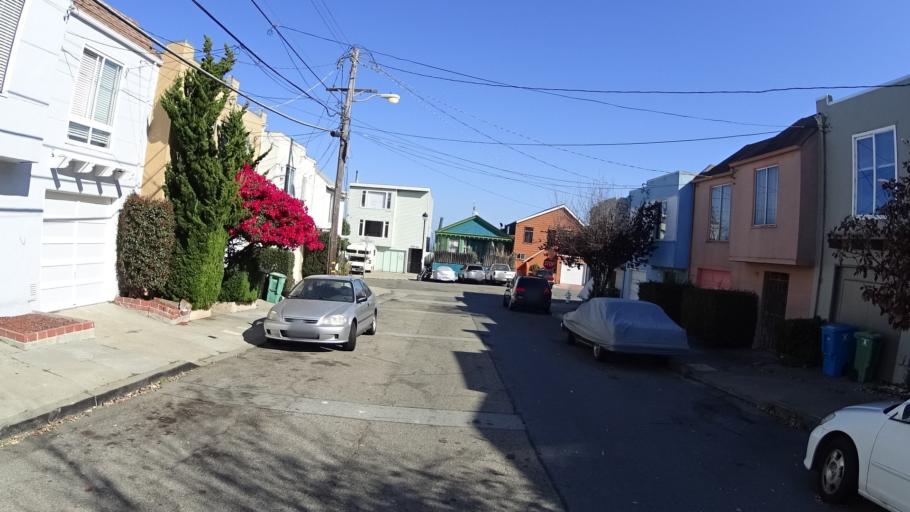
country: US
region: California
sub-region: San Francisco County
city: San Francisco
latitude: 37.7445
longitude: -122.4082
